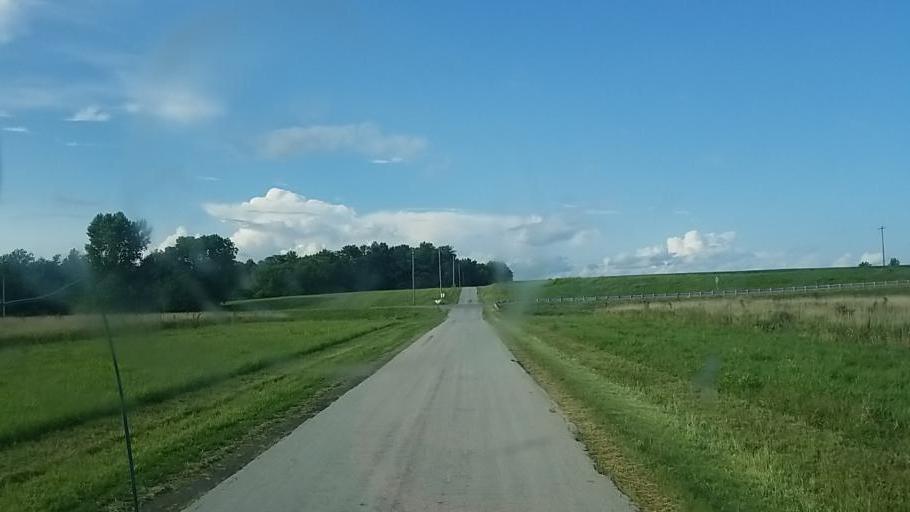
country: US
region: Ohio
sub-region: Wyandot County
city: Upper Sandusky
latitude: 40.8019
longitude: -83.3523
